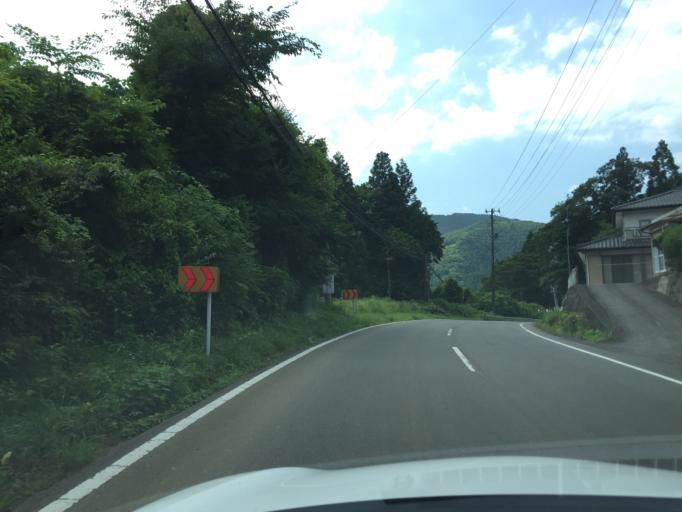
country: JP
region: Fukushima
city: Iwaki
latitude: 37.0574
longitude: 140.6910
